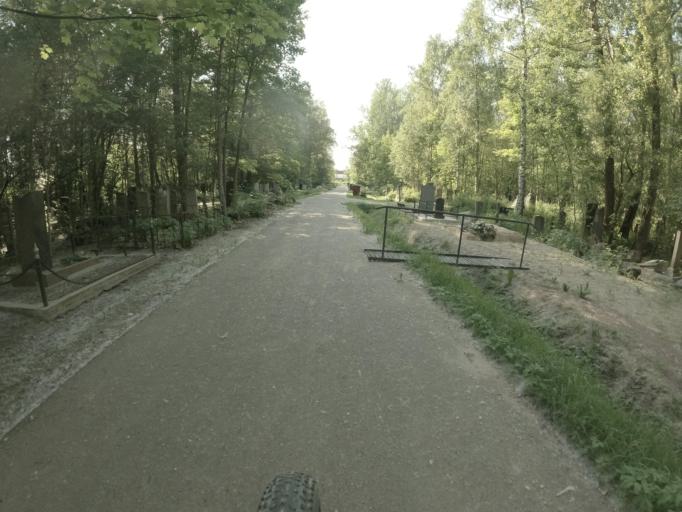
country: RU
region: St.-Petersburg
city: Obukhovo
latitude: 59.8536
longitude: 30.4516
